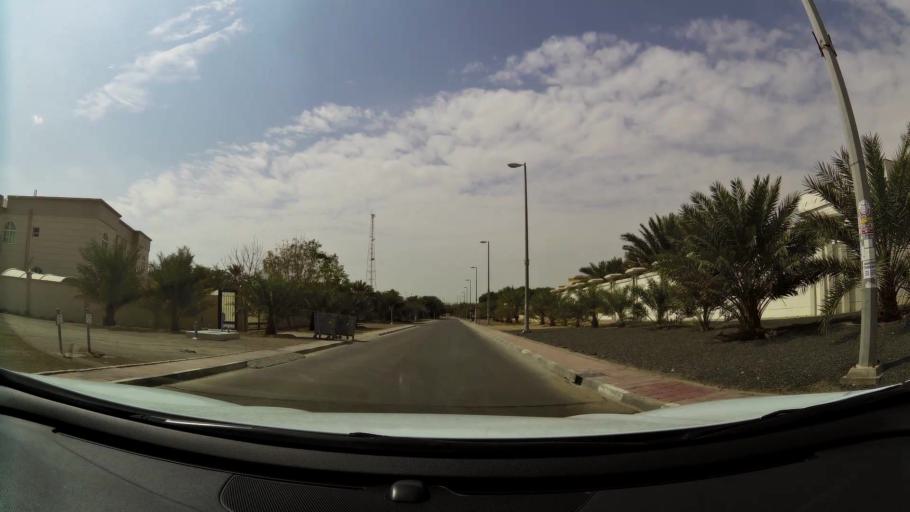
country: AE
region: Abu Dhabi
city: Al Ain
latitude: 24.1995
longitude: 55.7884
